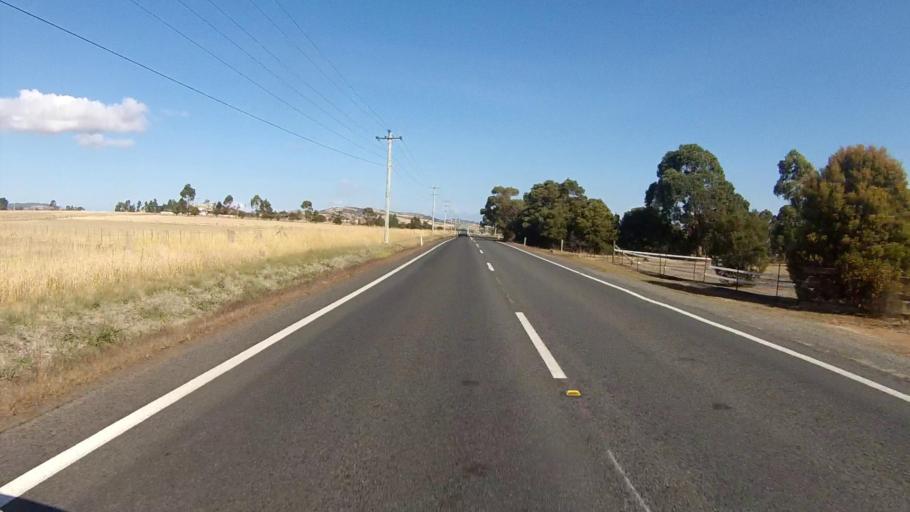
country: AU
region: Tasmania
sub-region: Sorell
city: Sorell
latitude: -42.7331
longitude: 147.5285
